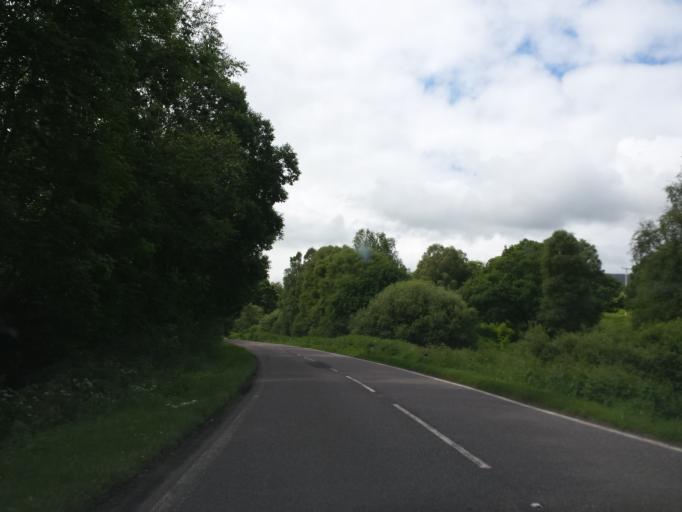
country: GB
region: Scotland
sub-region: Highland
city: Fort William
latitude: 56.8458
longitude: -5.1529
